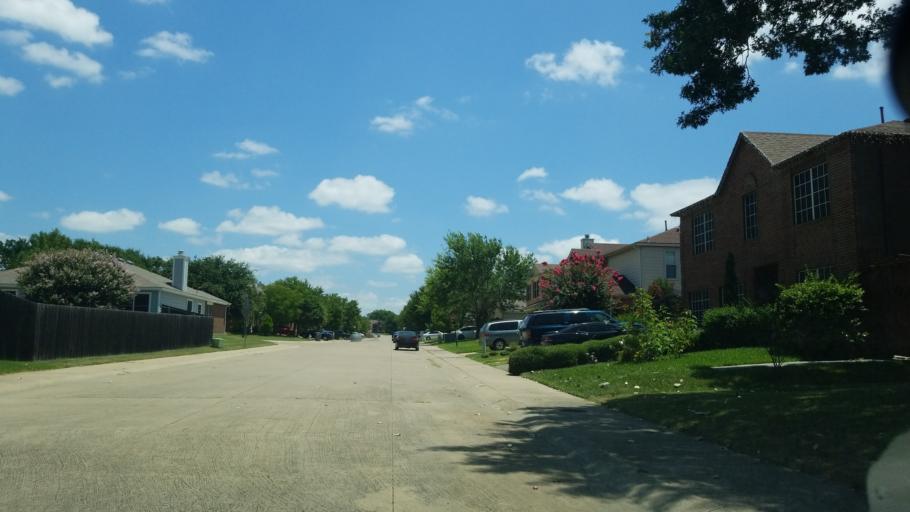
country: US
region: Texas
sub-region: Dallas County
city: Balch Springs
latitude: 32.7439
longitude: -96.7049
